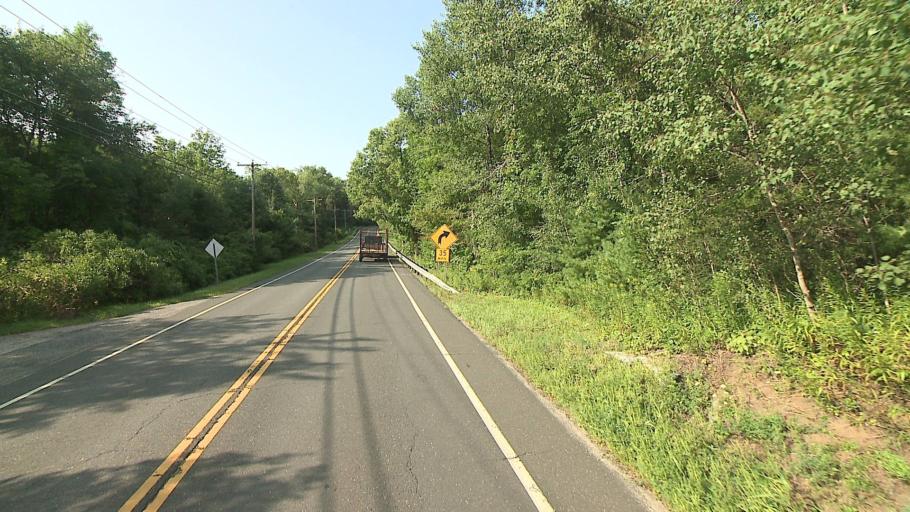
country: US
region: Connecticut
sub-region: Litchfield County
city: Canaan
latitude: 41.9589
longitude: -73.3453
